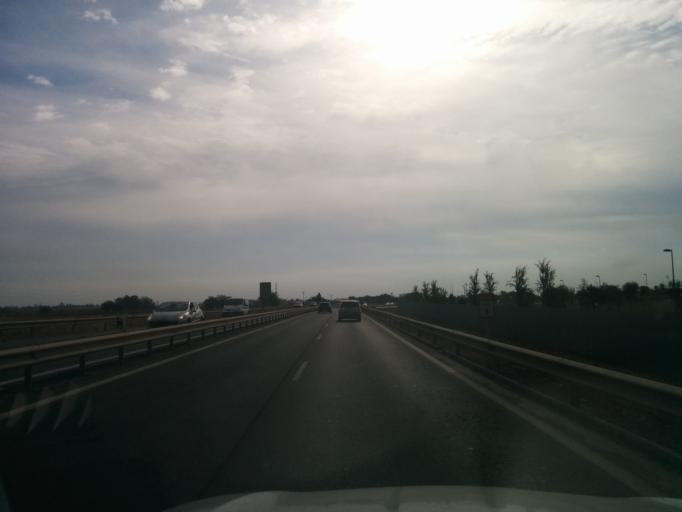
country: ES
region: Andalusia
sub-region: Provincia de Sevilla
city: La Algaba
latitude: 37.4356
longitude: -5.9706
